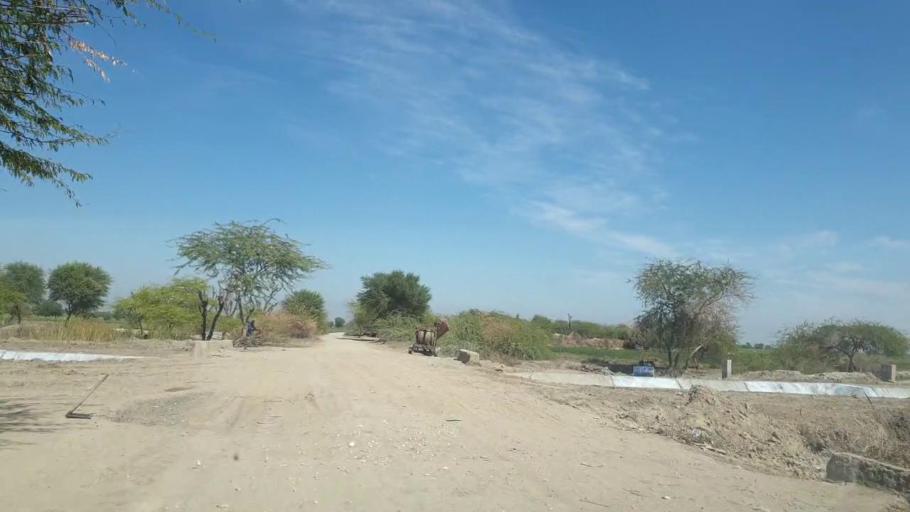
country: PK
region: Sindh
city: Pithoro
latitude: 25.6377
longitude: 69.2243
